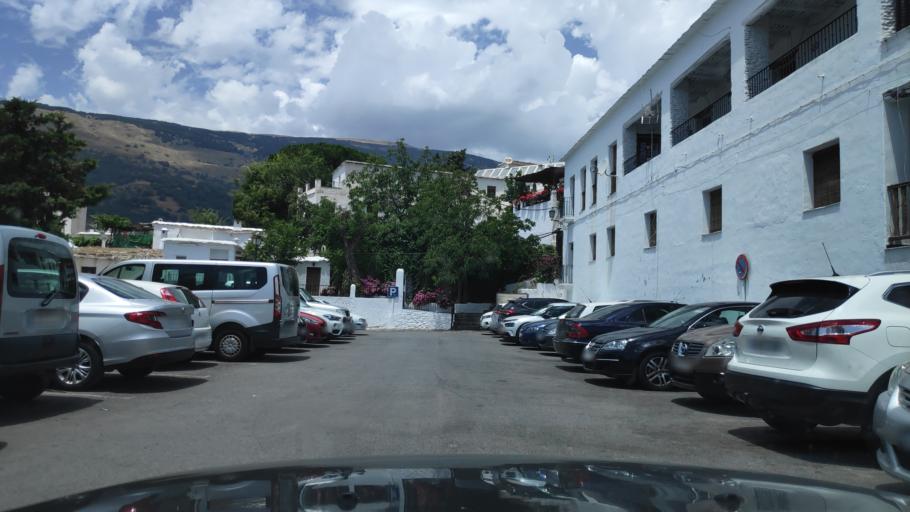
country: ES
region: Andalusia
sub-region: Provincia de Granada
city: Capileira
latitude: 36.9607
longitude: -3.3586
